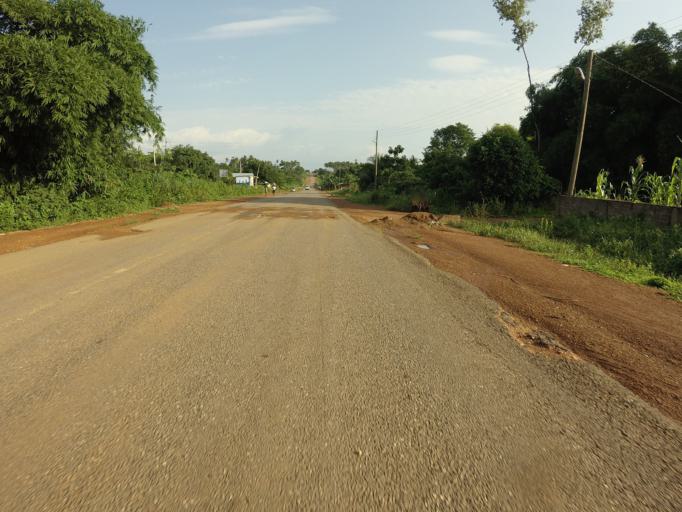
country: GH
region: Volta
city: Hohoe
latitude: 7.0525
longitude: 0.4273
